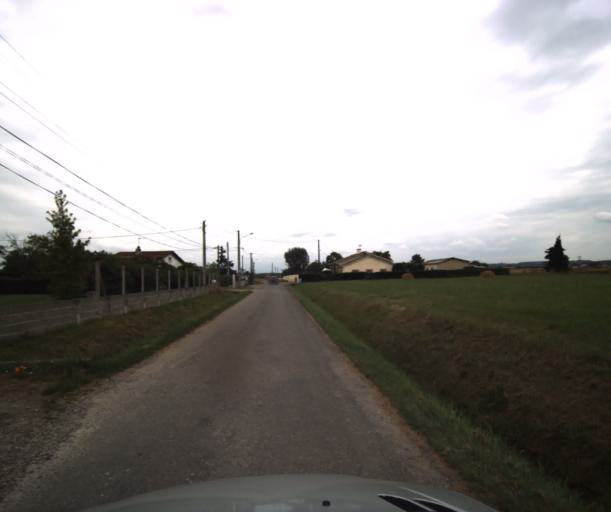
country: FR
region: Midi-Pyrenees
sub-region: Departement de la Haute-Garonne
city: Labarthe-sur-Leze
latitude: 43.4574
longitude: 1.3807
